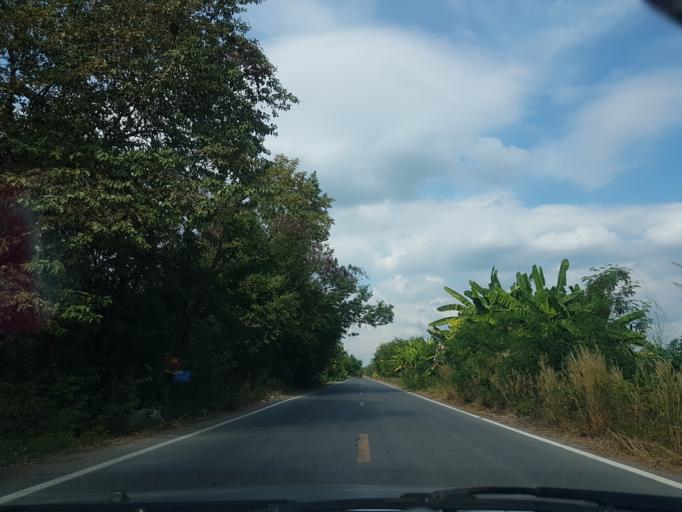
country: TH
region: Pathum Thani
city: Nong Suea
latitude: 14.1447
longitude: 100.8914
